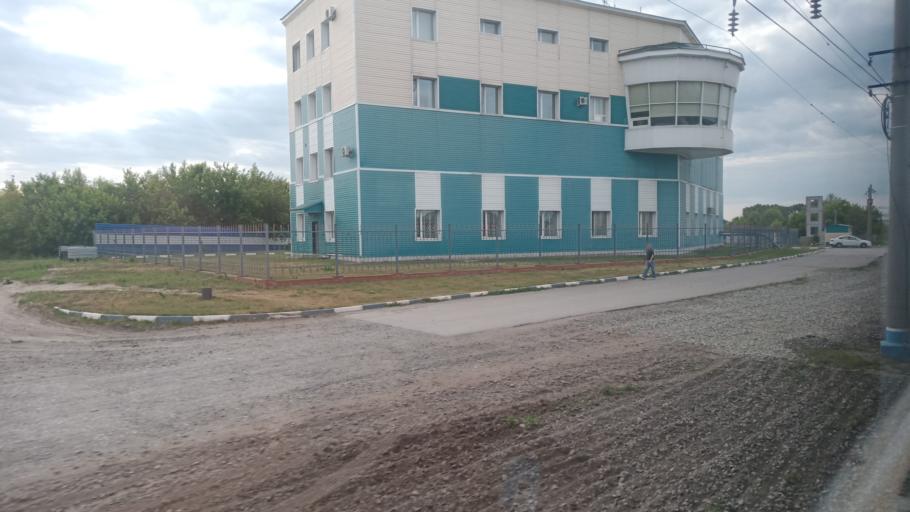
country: RU
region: Altai Krai
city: Novoaltaysk
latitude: 53.4146
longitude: 83.9163
